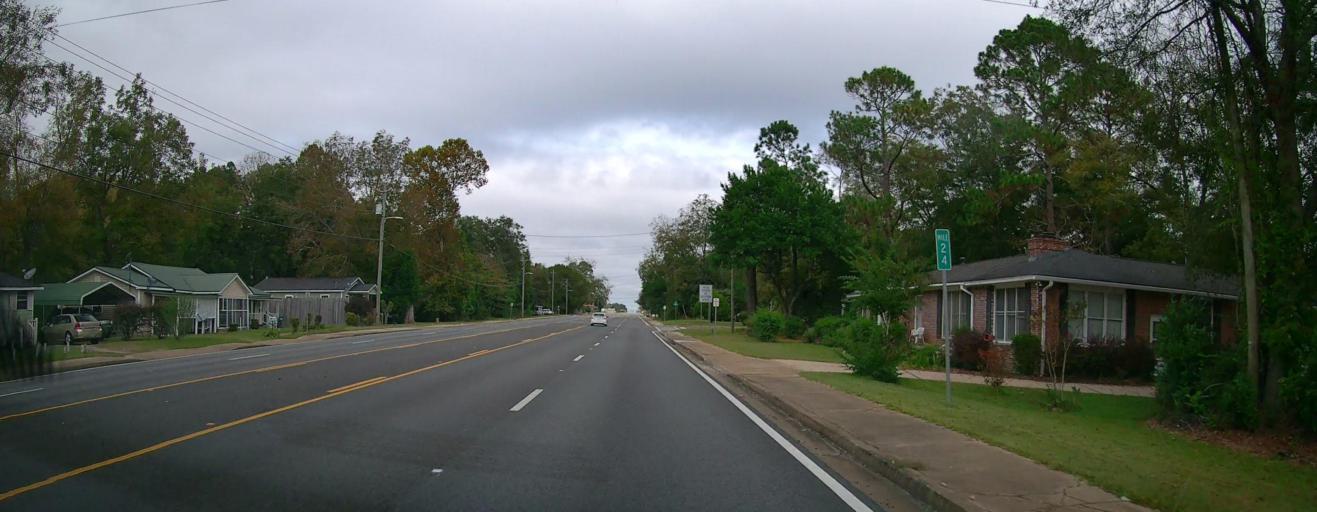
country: US
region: Georgia
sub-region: Colquitt County
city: Moultrie
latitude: 31.0040
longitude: -83.8688
